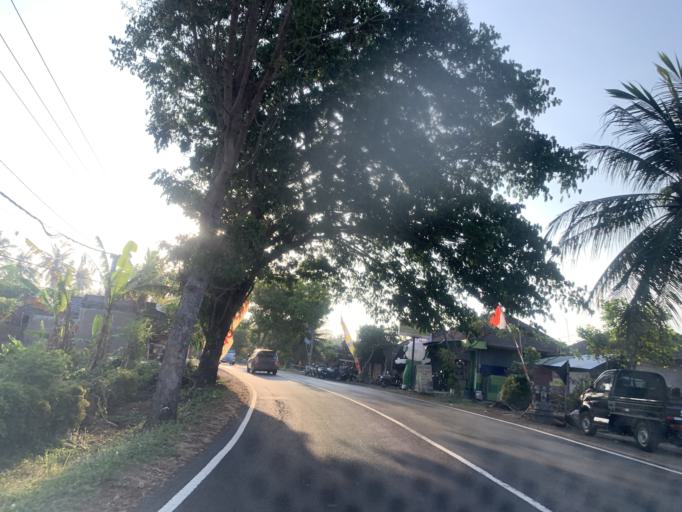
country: ID
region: Bali
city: Banjar Delodrurung
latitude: -8.4925
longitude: 114.9600
